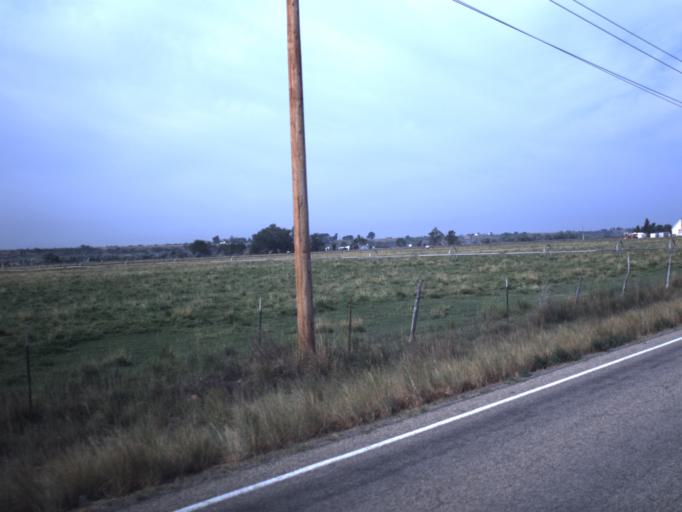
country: US
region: Utah
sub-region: Duchesne County
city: Roosevelt
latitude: 40.2585
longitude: -110.0991
